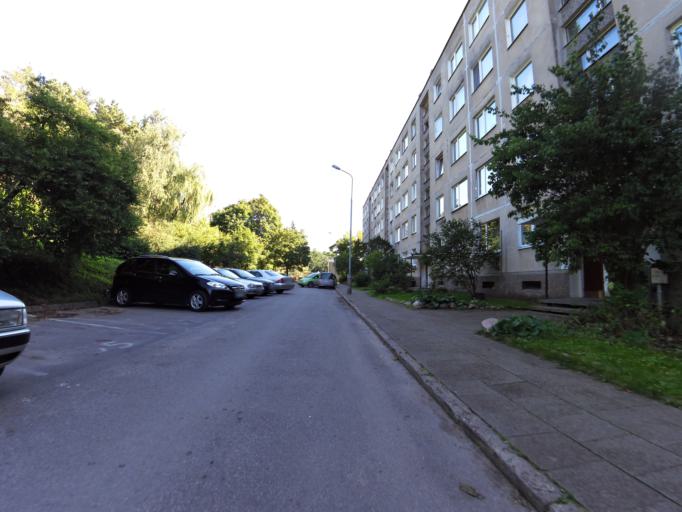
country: LT
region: Vilnius County
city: Lazdynai
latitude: 54.6850
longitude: 25.2145
